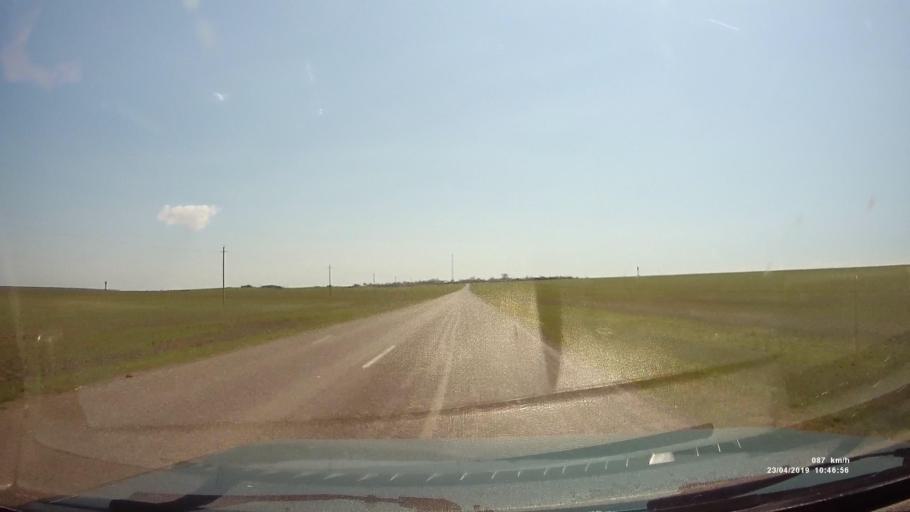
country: RU
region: Kalmykiya
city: Yashalta
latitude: 46.4390
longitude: 42.6992
